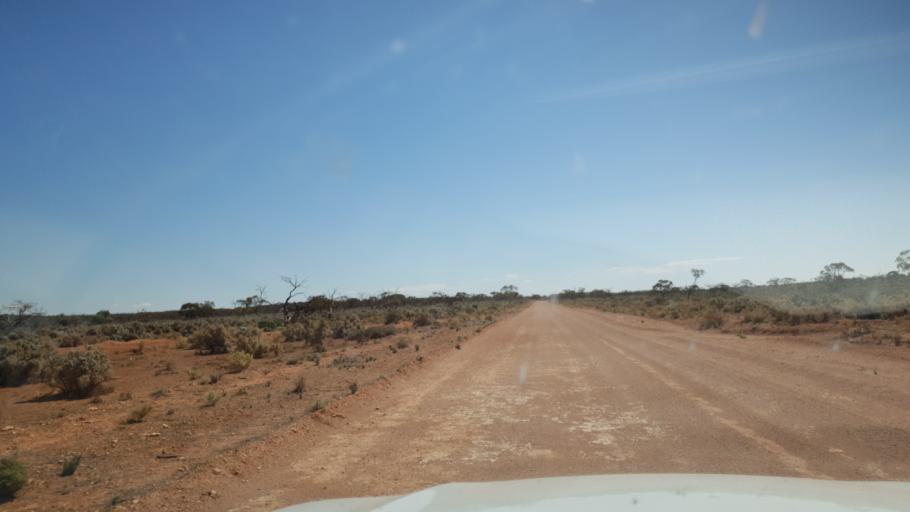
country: AU
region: South Australia
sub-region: Kimba
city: Caralue
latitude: -32.4897
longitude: 136.4522
